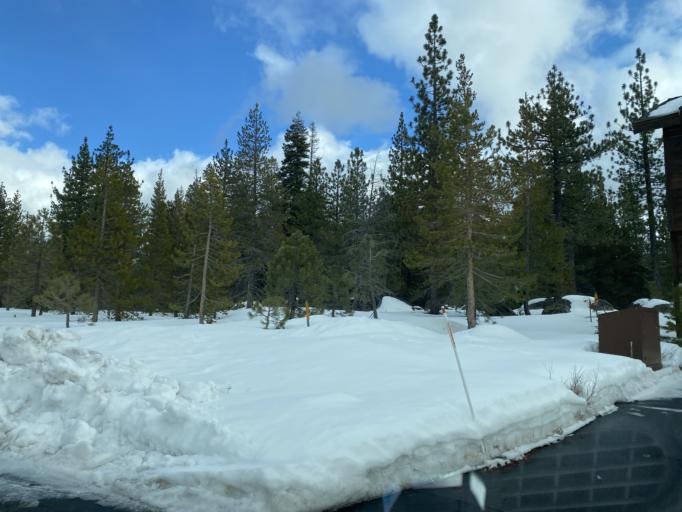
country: US
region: California
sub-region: El Dorado County
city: South Lake Tahoe
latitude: 38.8489
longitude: -120.0236
